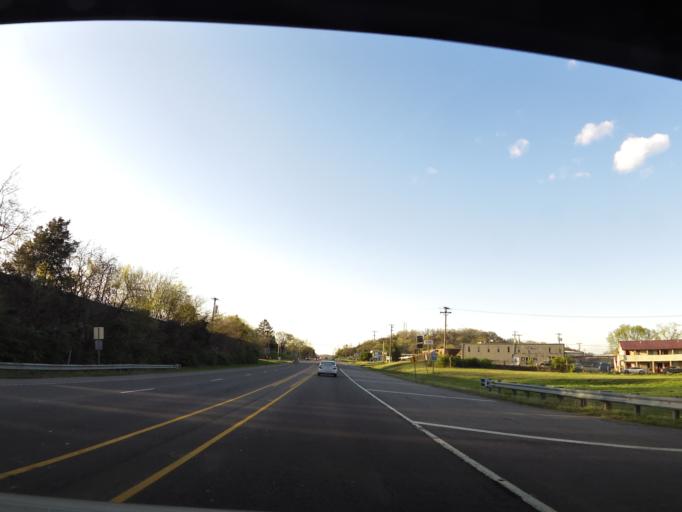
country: US
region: Tennessee
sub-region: Davidson County
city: Goodlettsville
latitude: 36.3431
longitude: -86.7194
